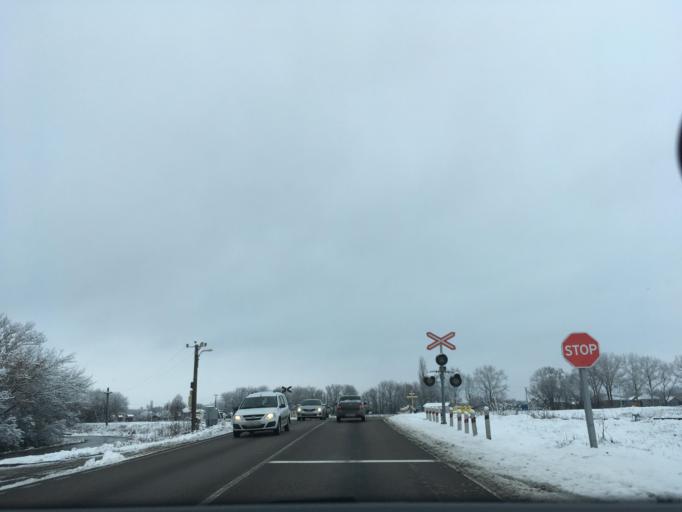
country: RU
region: Voronezj
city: Zabolotovka
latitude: 50.2469
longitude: 39.3518
